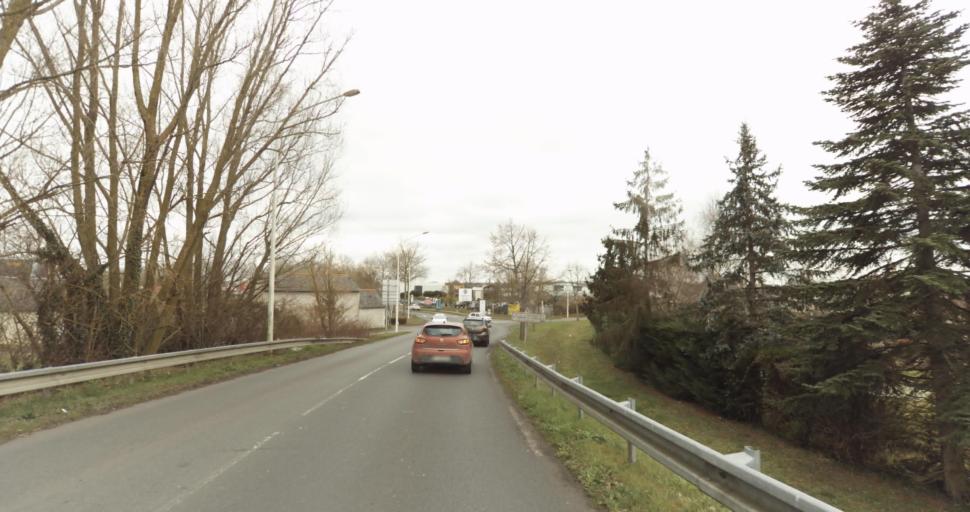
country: FR
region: Pays de la Loire
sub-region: Departement de Maine-et-Loire
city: Saumur
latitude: 47.2799
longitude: -0.0679
